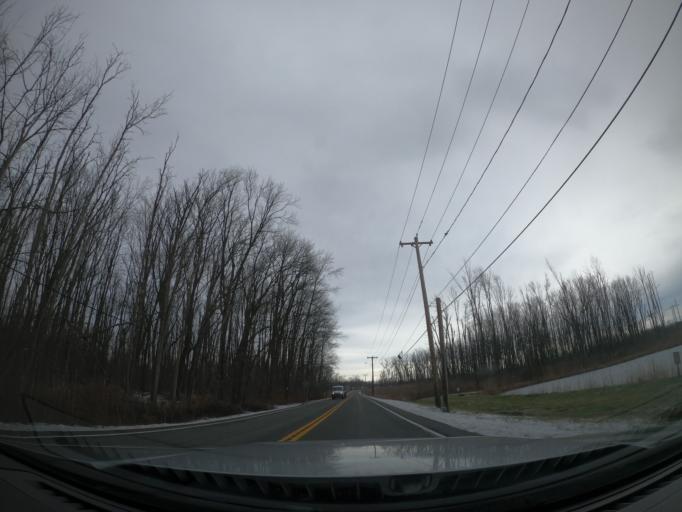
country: US
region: New York
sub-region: Onondaga County
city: Minoa
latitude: 43.1068
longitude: -76.0442
